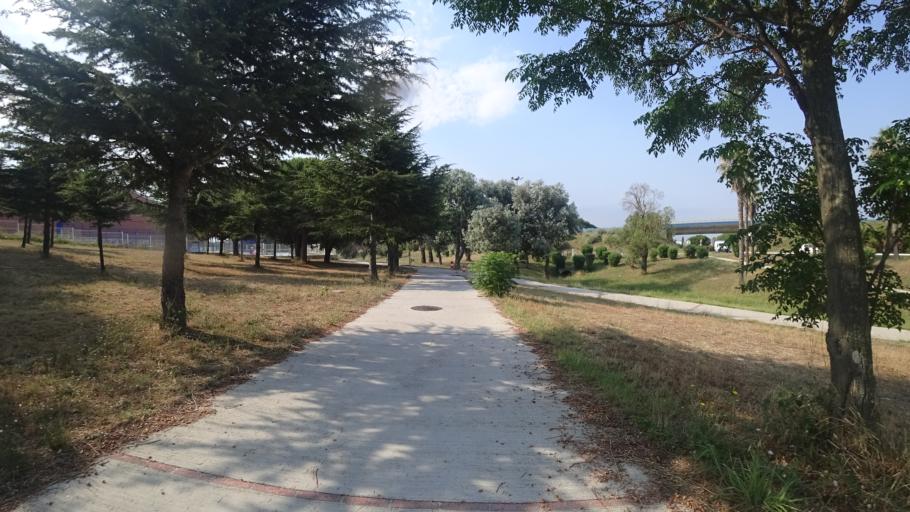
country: FR
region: Languedoc-Roussillon
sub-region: Departement des Pyrenees-Orientales
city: Canet-en-Roussillon
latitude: 42.7033
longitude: 3.0167
